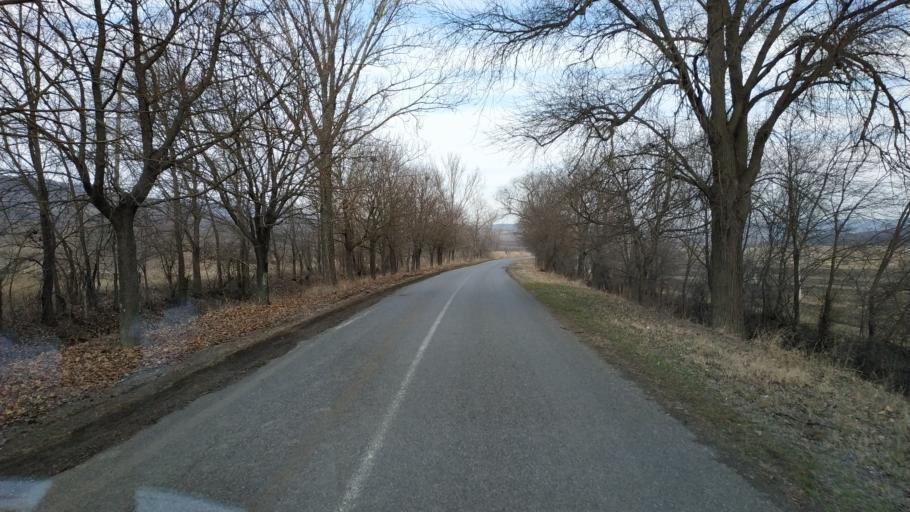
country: MD
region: Nisporeni
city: Nisporeni
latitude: 47.1011
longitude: 28.1283
